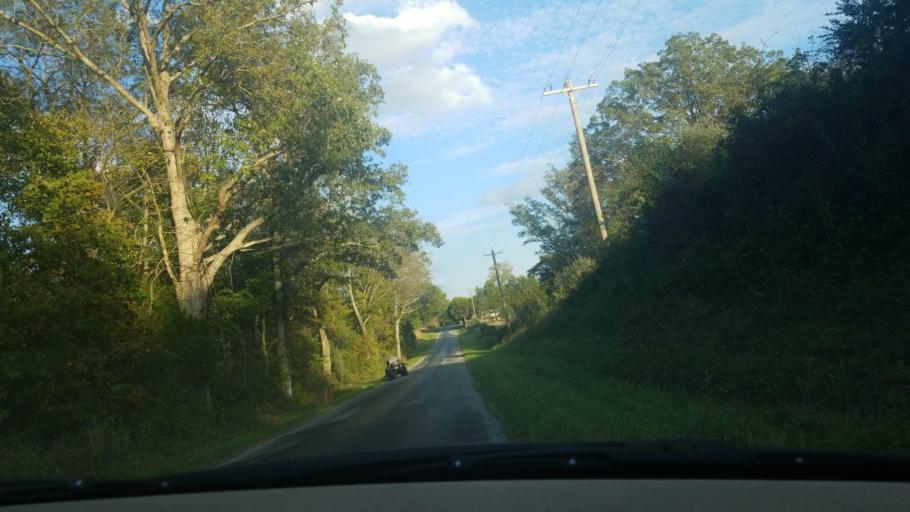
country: US
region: Illinois
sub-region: Saline County
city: Carrier Mills
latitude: 37.7720
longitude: -88.7244
